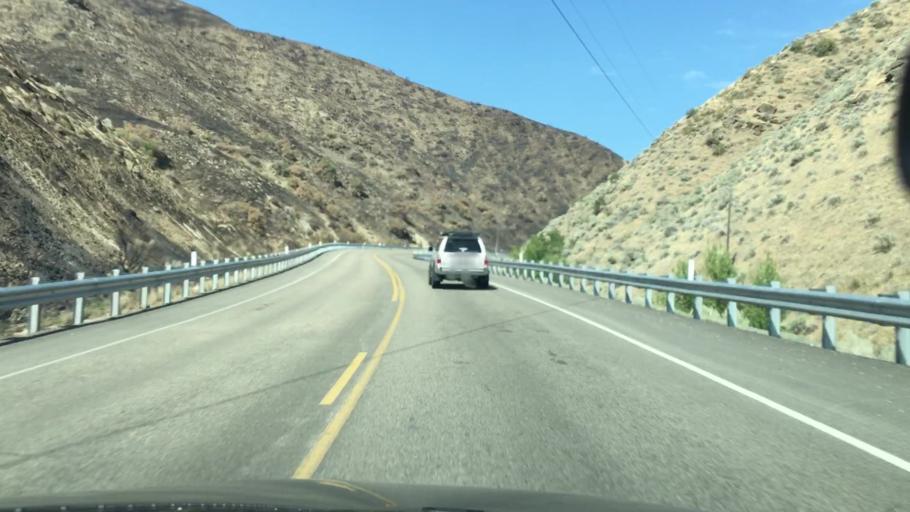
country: US
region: Idaho
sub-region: Ada County
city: Eagle
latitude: 43.7592
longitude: -116.2748
